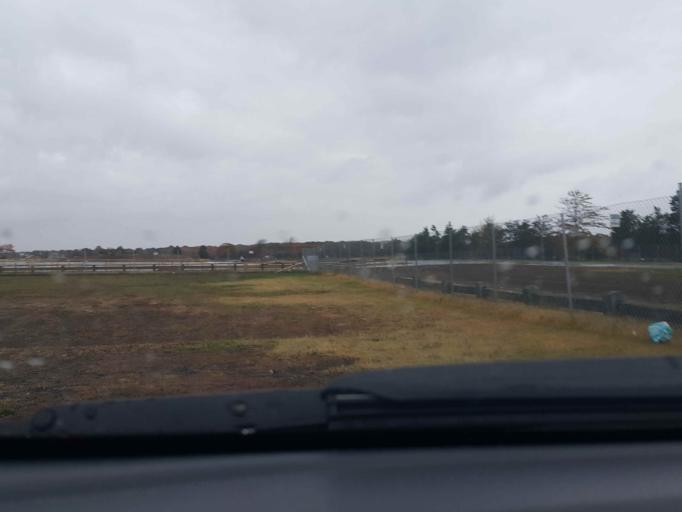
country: US
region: Connecticut
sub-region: Middlesex County
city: Clinton
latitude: 41.2634
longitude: -72.5584
